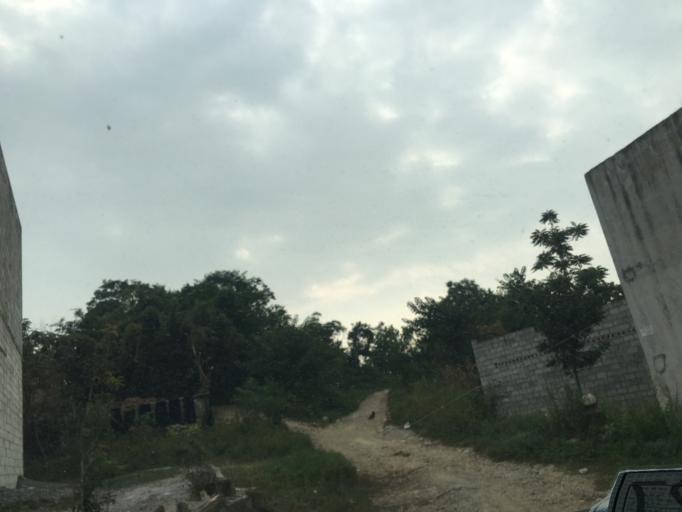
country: CN
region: Guangxi Zhuangzu Zizhiqu
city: Xinzhou
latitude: 25.4451
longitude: 105.6467
